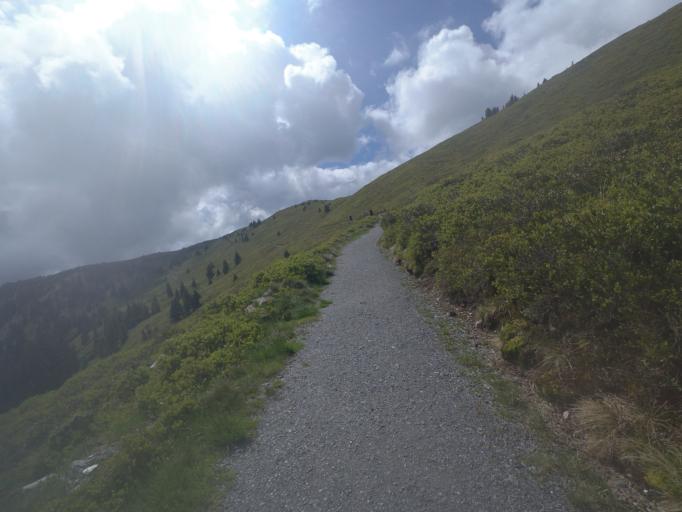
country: AT
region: Salzburg
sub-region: Politischer Bezirk Zell am See
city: Viehhofen
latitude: 47.3958
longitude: 12.7081
